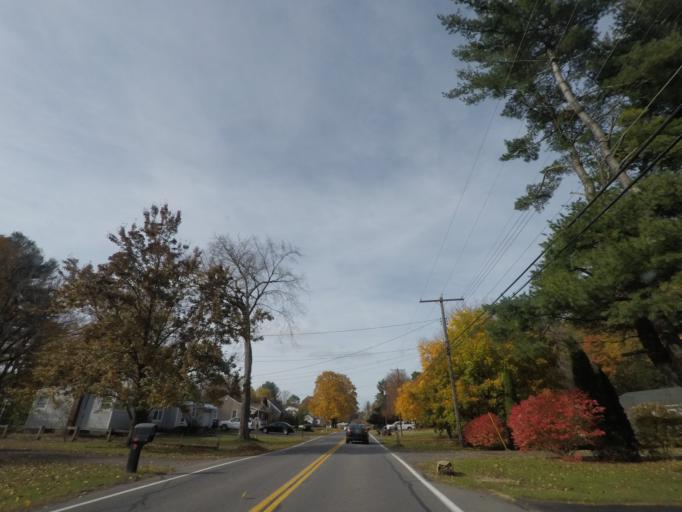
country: US
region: New York
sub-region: Schenectady County
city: Rotterdam
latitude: 42.7512
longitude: -73.9377
